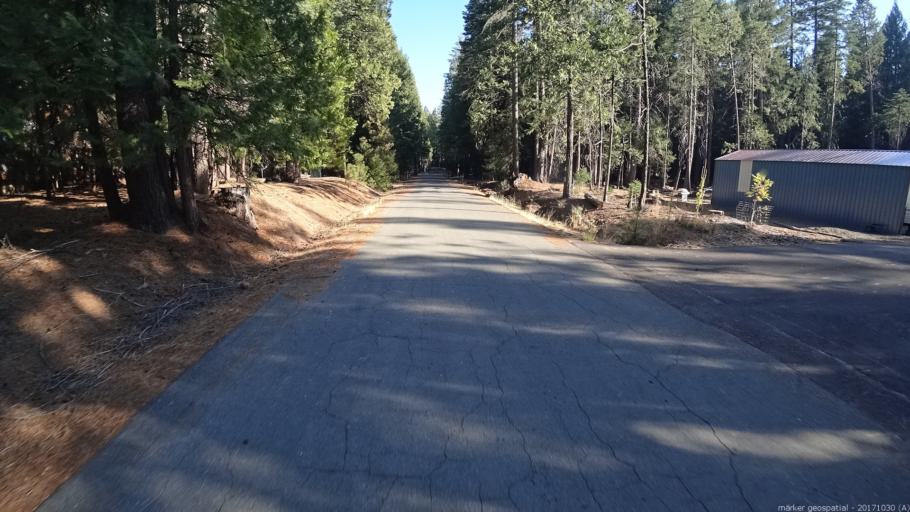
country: US
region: California
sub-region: Shasta County
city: Shingletown
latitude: 40.5532
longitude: -121.7296
